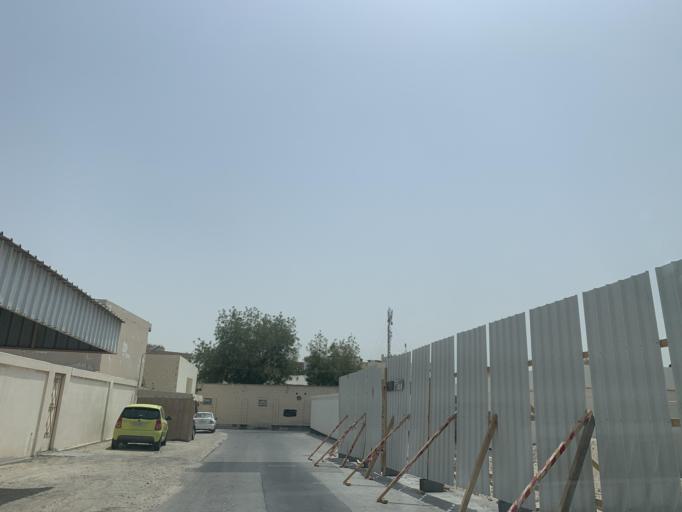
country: BH
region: Northern
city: Madinat `Isa
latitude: 26.1807
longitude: 50.5519
